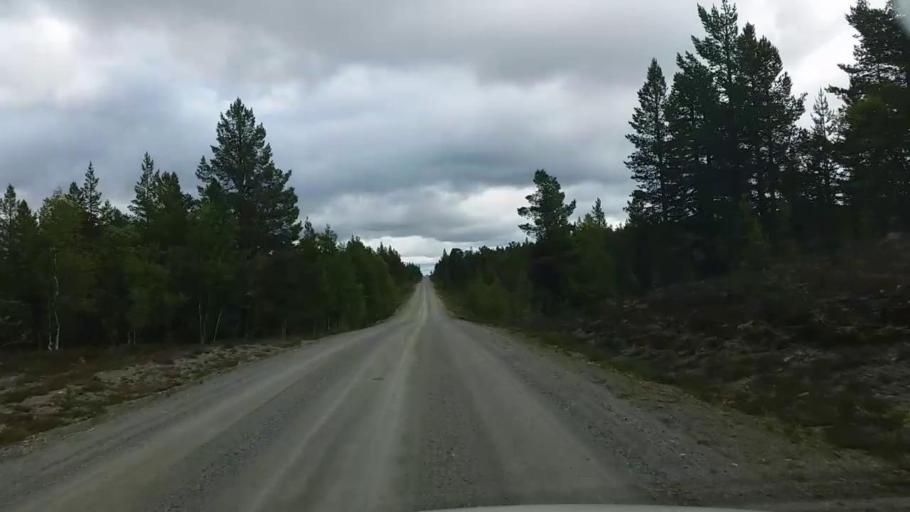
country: NO
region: Hedmark
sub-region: Engerdal
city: Engerdal
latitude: 62.3387
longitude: 12.6191
